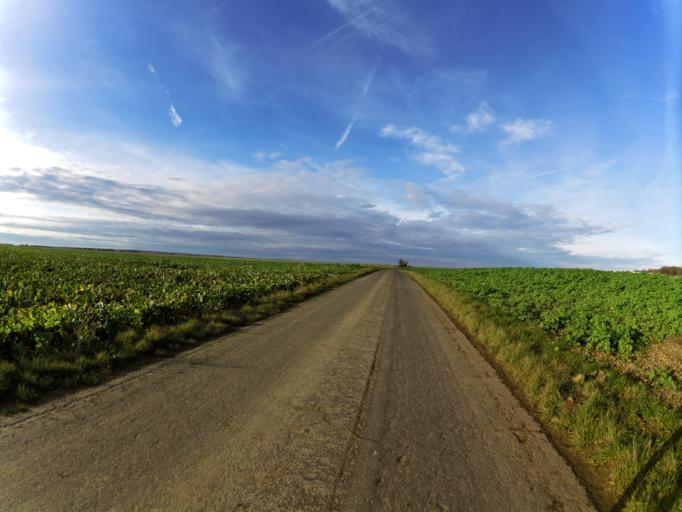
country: DE
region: Bavaria
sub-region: Regierungsbezirk Unterfranken
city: Giebelstadt
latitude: 49.6824
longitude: 9.9396
